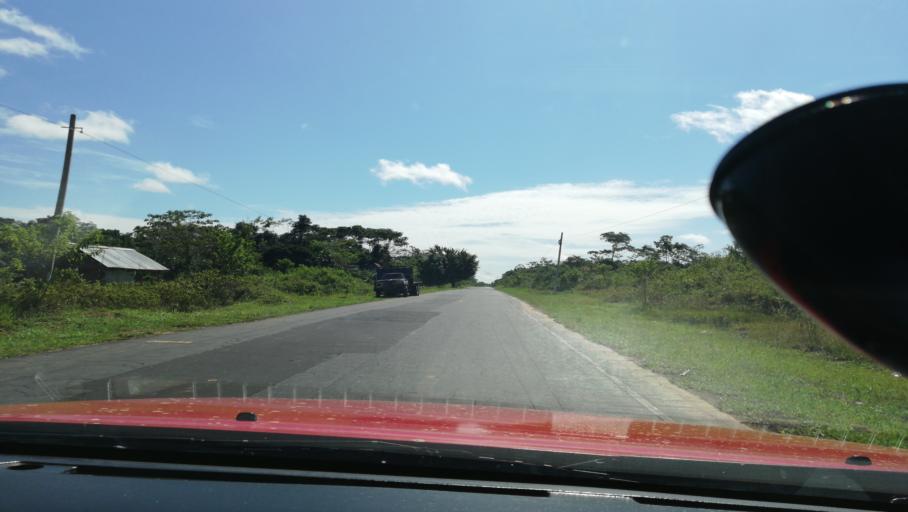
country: PE
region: Loreto
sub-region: Provincia de Loreto
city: Nauta
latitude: -4.3220
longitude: -73.5286
